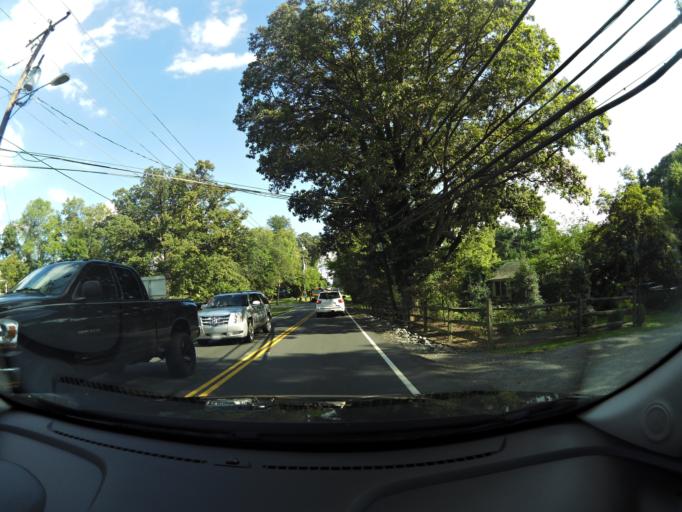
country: US
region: Virginia
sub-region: Fairfax County
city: Great Falls
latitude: 38.9970
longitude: -77.2857
